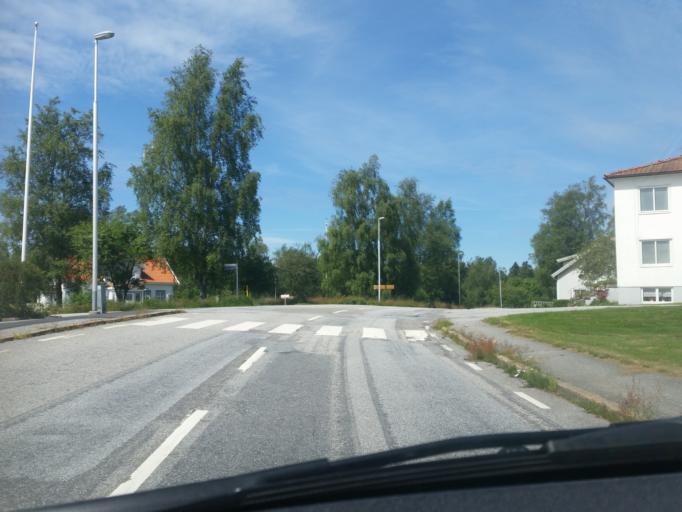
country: SE
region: Vaestra Goetaland
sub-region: Tanums Kommun
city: Tanumshede
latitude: 58.6100
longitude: 11.4735
